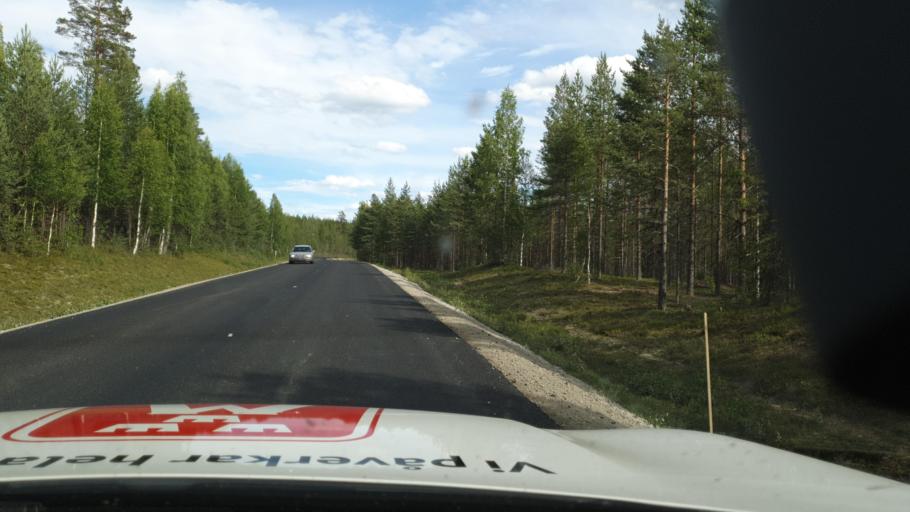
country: SE
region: Vaesterbotten
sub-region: Lycksele Kommun
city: Lycksele
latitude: 64.8195
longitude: 18.8586
